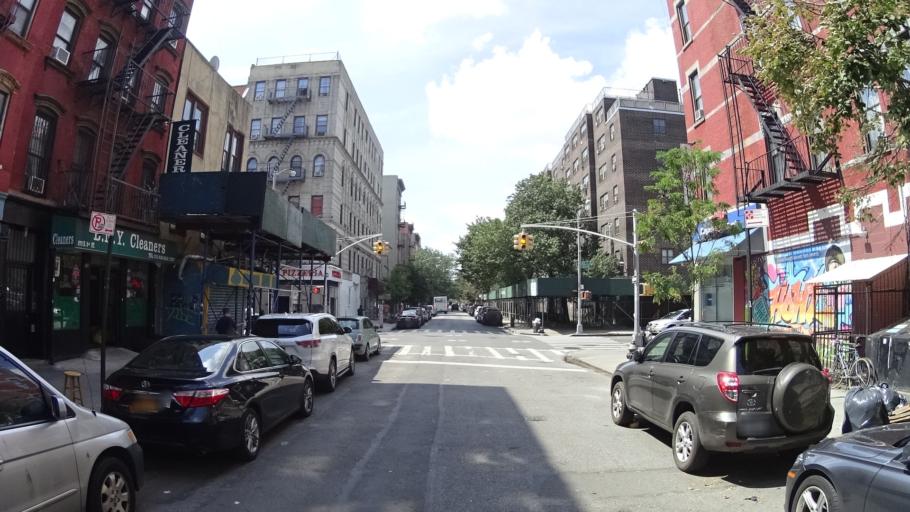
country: US
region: New York
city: New York City
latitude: 40.7215
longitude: -73.9801
